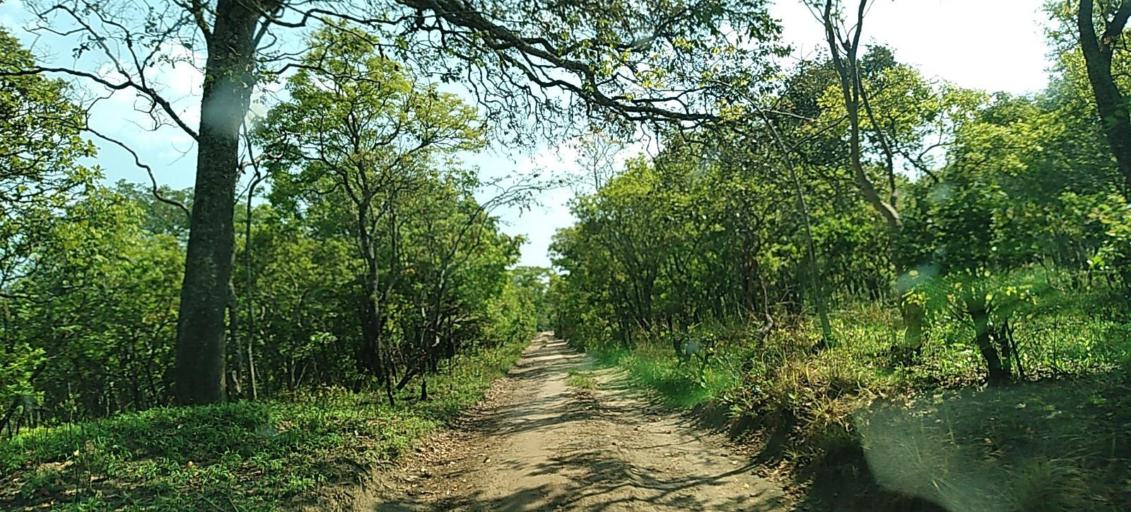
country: ZM
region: North-Western
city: Mwinilunga
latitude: -11.2816
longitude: 24.9247
